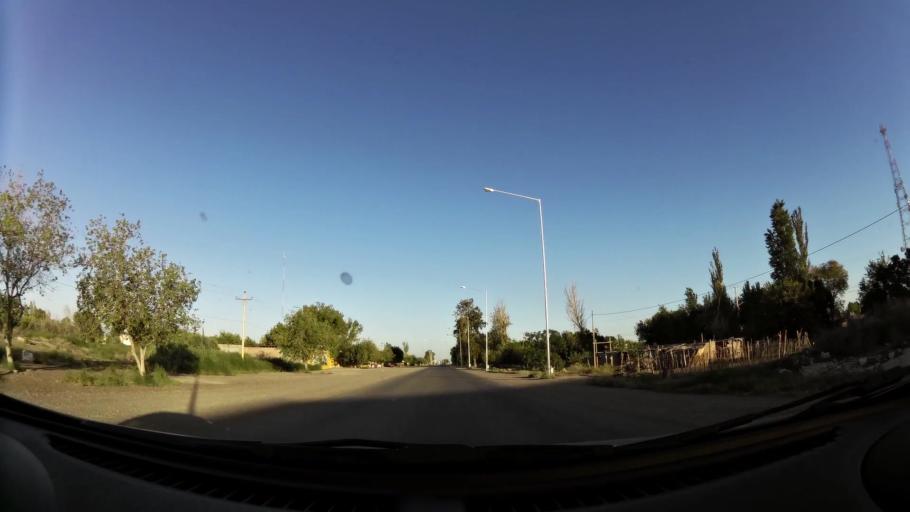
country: AR
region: San Juan
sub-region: Departamento de Santa Lucia
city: Santa Lucia
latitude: -31.5504
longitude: -68.4812
